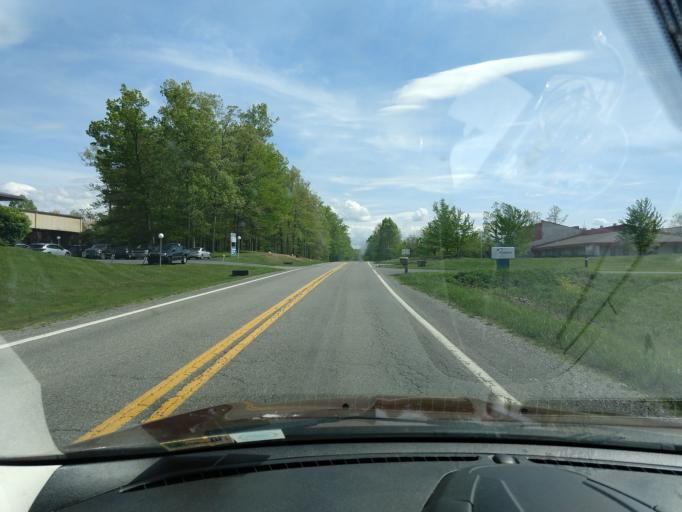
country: US
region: West Virginia
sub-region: Raleigh County
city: Stanaford
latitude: 37.7892
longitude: -81.1167
